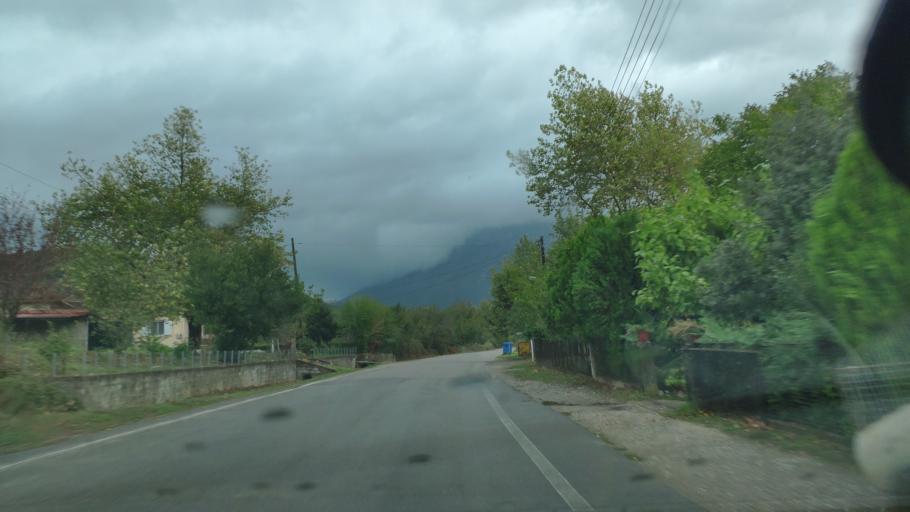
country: GR
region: West Greece
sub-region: Nomos Aitolias kai Akarnanias
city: Krikellos
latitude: 39.0037
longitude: 21.3089
